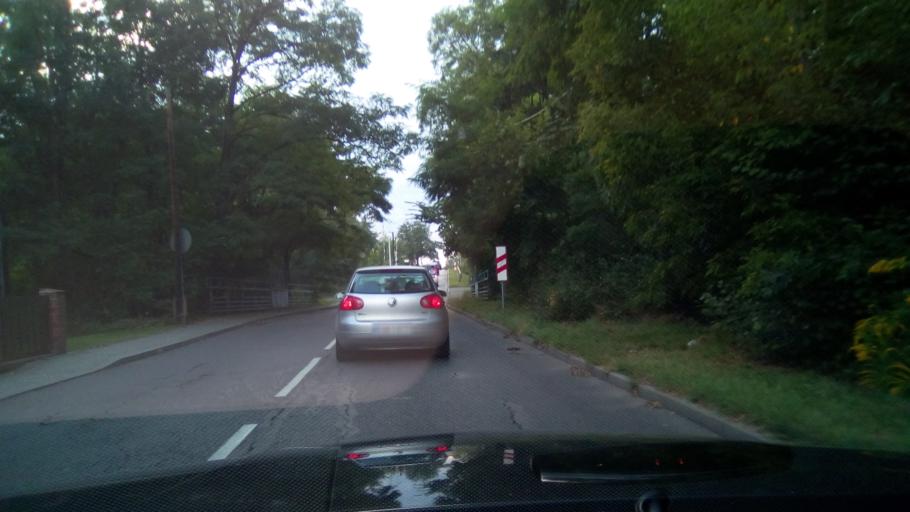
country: PL
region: Silesian Voivodeship
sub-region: Myslowice
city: Myslowice
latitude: 50.2072
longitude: 19.1517
